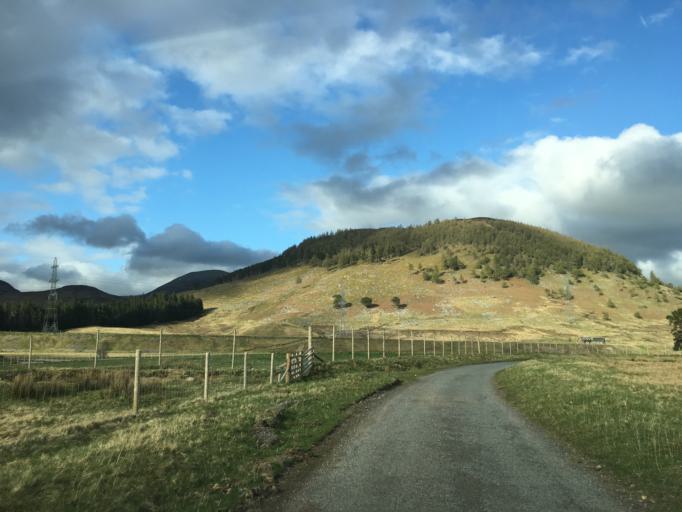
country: GB
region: Scotland
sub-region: Highland
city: Kingussie
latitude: 57.0203
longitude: -4.4357
